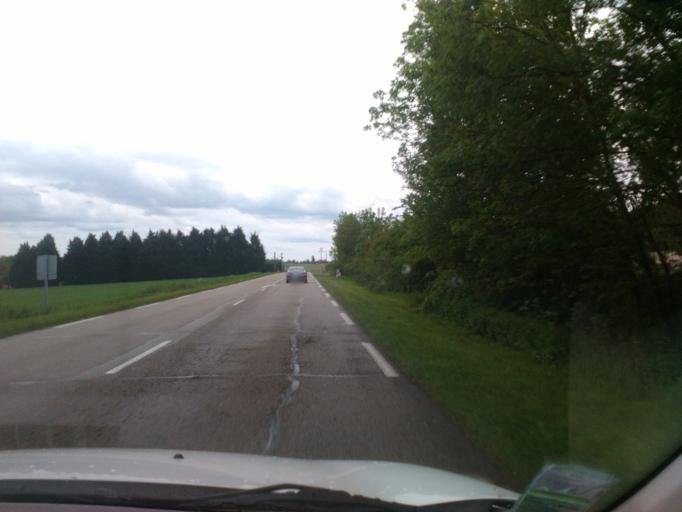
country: FR
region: Champagne-Ardenne
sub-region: Departement de l'Aube
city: Lusigny-sur-Barse
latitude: 48.2422
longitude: 4.3623
